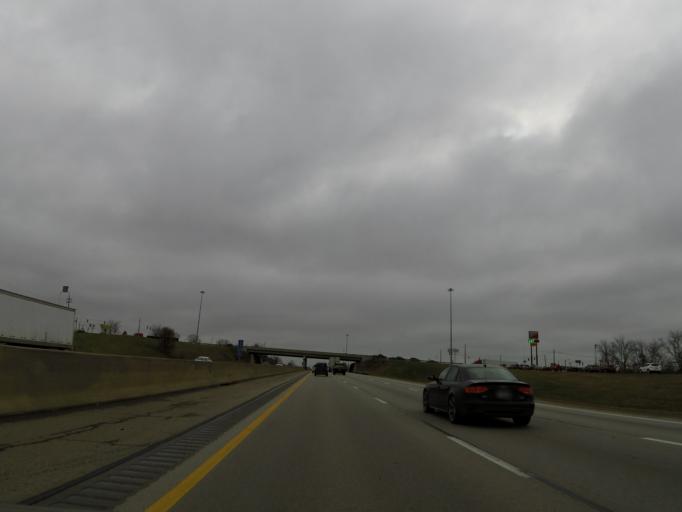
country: US
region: Kentucky
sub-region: Boone County
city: Walton
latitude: 38.8612
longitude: -84.6233
